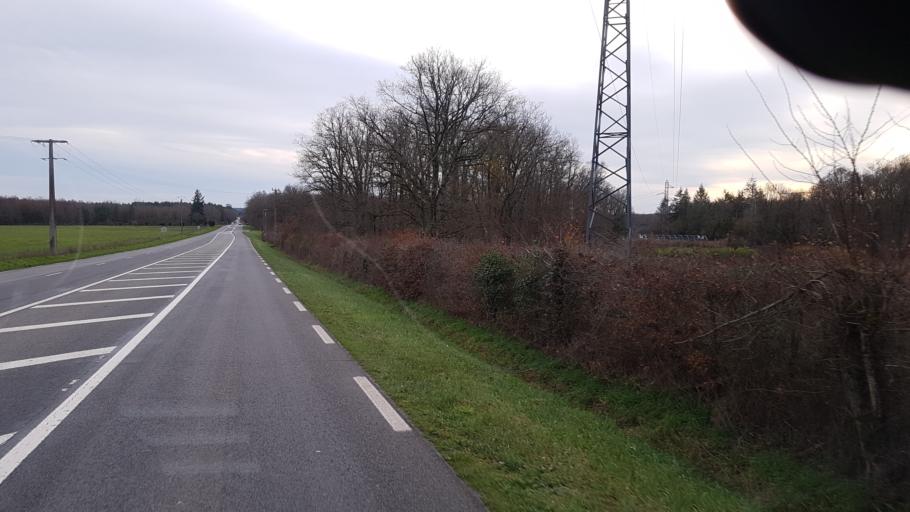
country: FR
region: Centre
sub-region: Departement du Loir-et-Cher
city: Nouan-le-Fuzelier
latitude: 47.5584
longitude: 2.0324
